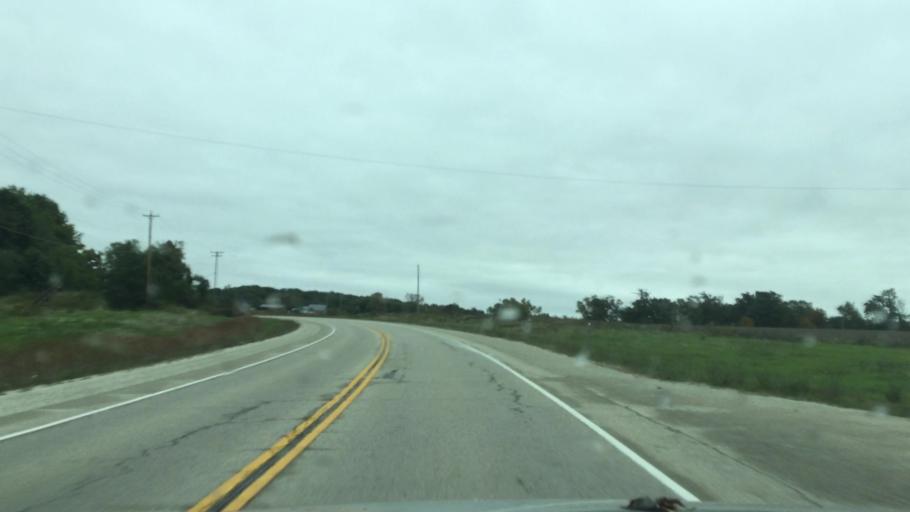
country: US
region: Wisconsin
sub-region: Racine County
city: Eagle Lake
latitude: 42.7393
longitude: -88.0957
